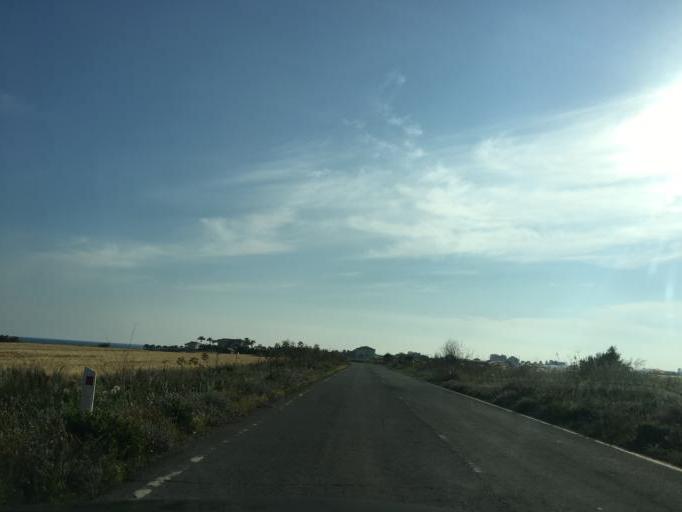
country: CY
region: Larnaka
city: Kofinou
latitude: 34.7414
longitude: 33.3806
